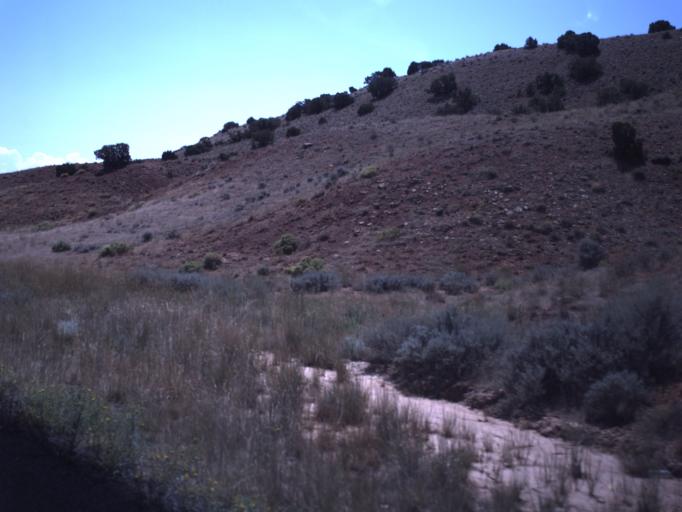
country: US
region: Utah
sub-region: Uintah County
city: Maeser
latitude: 40.4097
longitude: -109.7074
